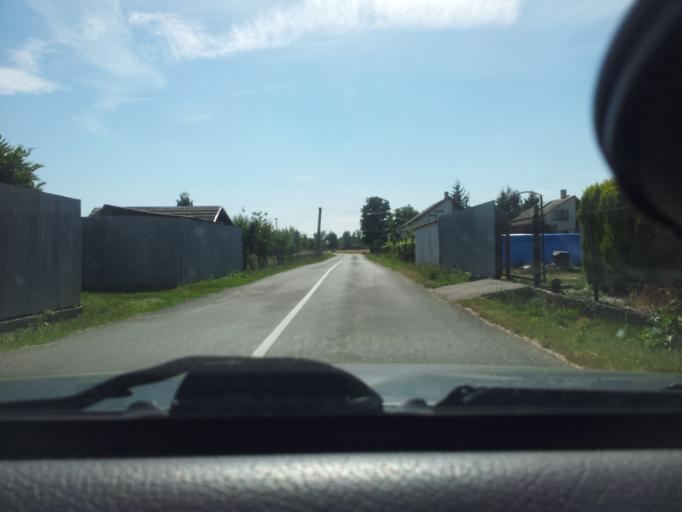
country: SK
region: Nitriansky
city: Tlmace
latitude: 48.2666
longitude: 18.5407
